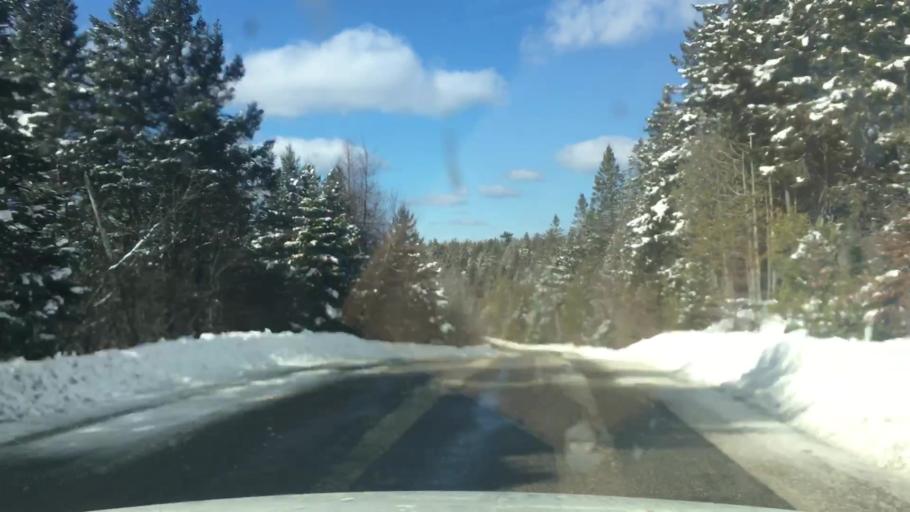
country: US
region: Maine
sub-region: Washington County
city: Machias
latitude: 44.6821
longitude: -67.4564
